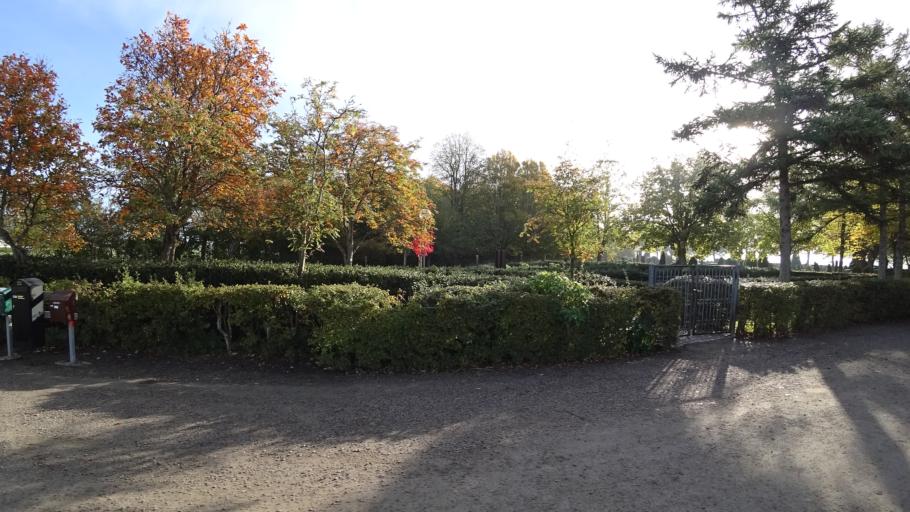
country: SE
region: Skane
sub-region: Staffanstorps Kommun
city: Staffanstorp
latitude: 55.6326
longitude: 13.2291
